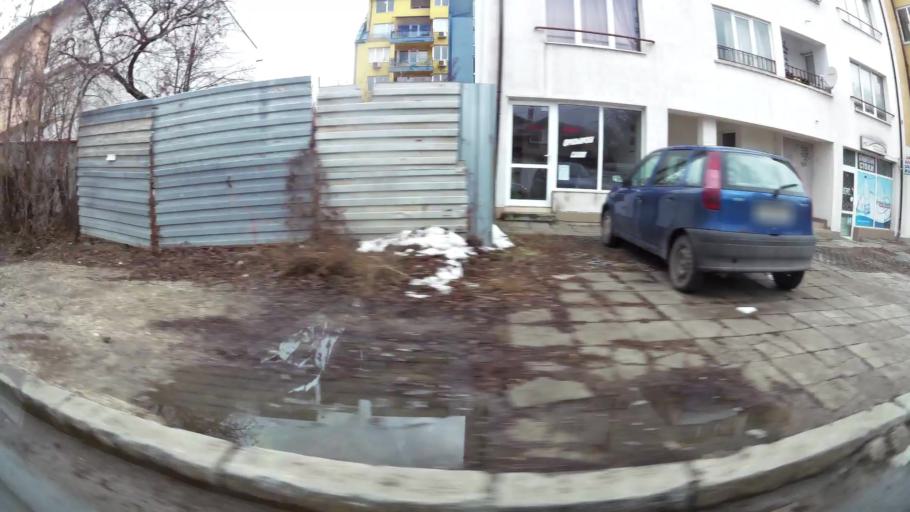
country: BG
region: Sofia-Capital
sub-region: Stolichna Obshtina
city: Sofia
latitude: 42.7220
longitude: 23.3062
